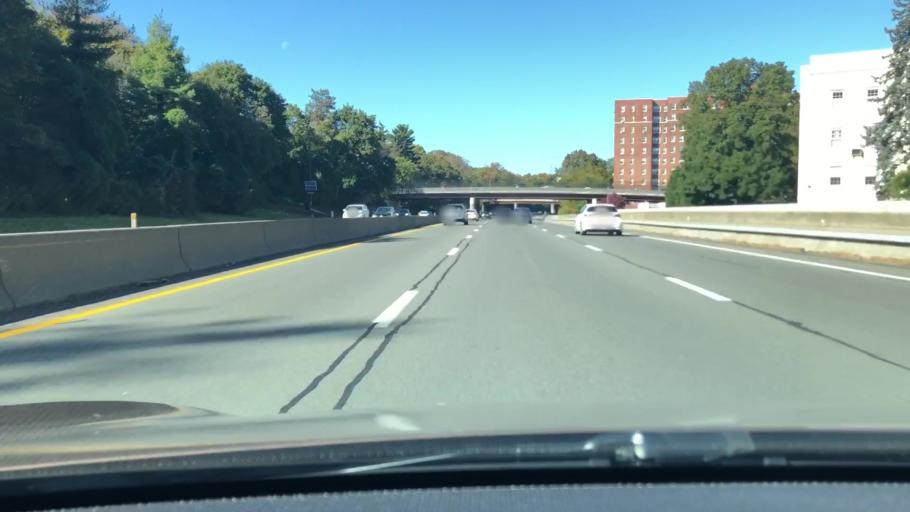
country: US
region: New York
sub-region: Westchester County
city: Bronxville
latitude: 40.9390
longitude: -73.8398
